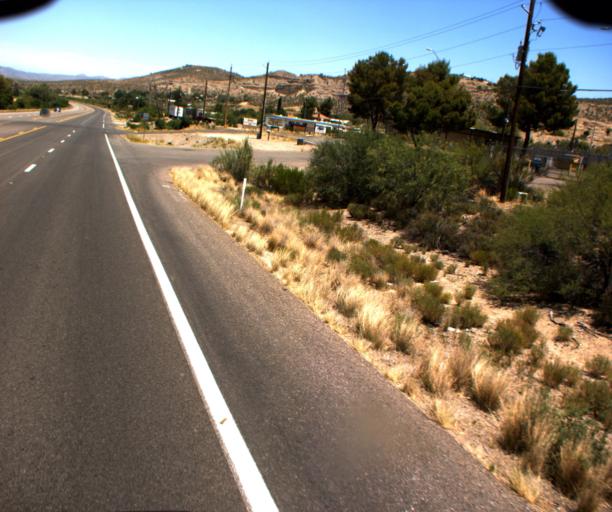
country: US
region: Arizona
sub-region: Gila County
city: Claypool
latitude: 33.4197
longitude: -110.8257
